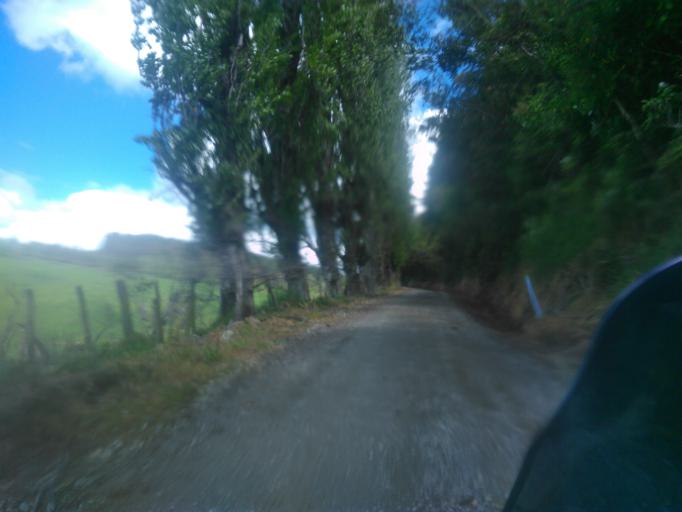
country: NZ
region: Hawke's Bay
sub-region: Wairoa District
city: Wairoa
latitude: -38.7667
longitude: 177.5942
